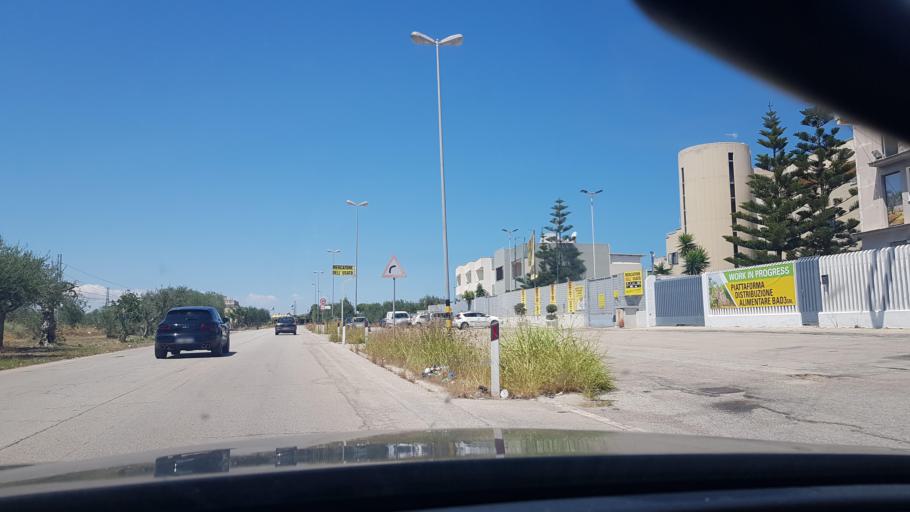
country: IT
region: Apulia
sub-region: Provincia di Barletta - Andria - Trani
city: Barletta
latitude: 41.3025
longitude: 16.3246
